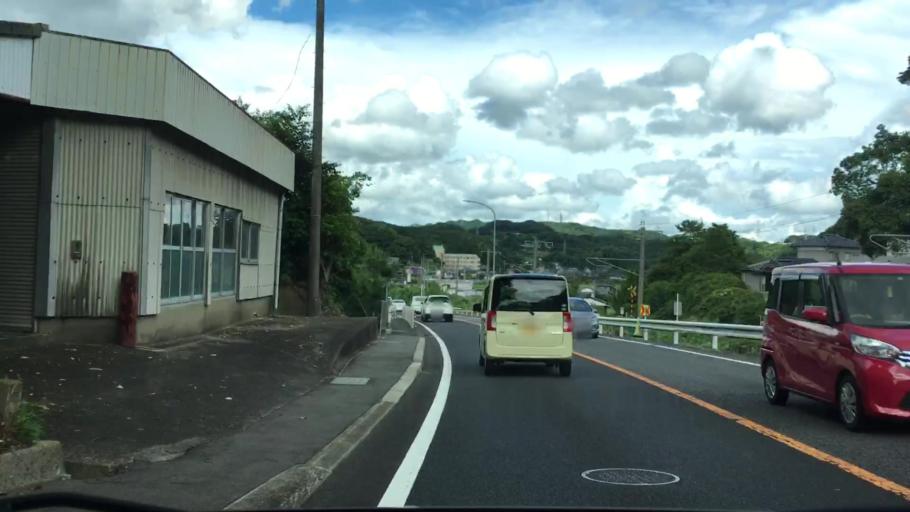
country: JP
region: Nagasaki
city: Sasebo
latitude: 33.1442
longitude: 129.8148
